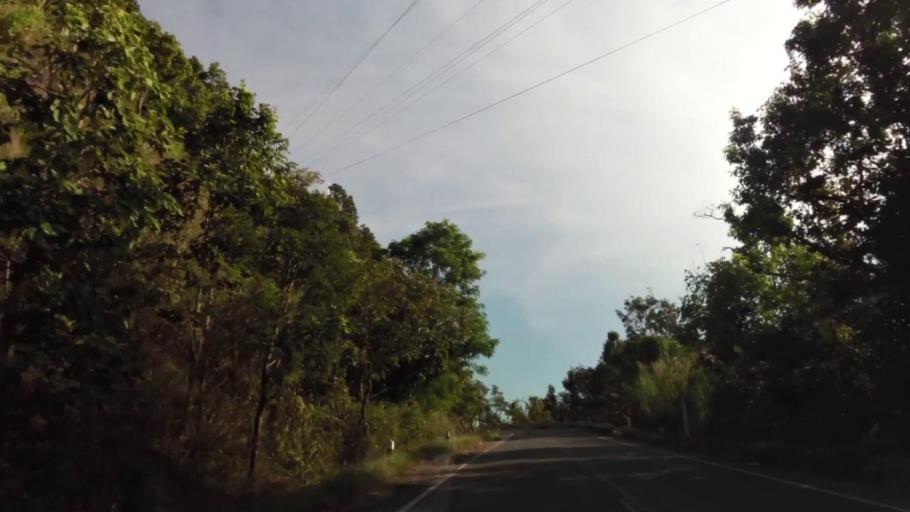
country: TH
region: Chiang Rai
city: Khun Tan
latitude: 19.8772
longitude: 100.3145
